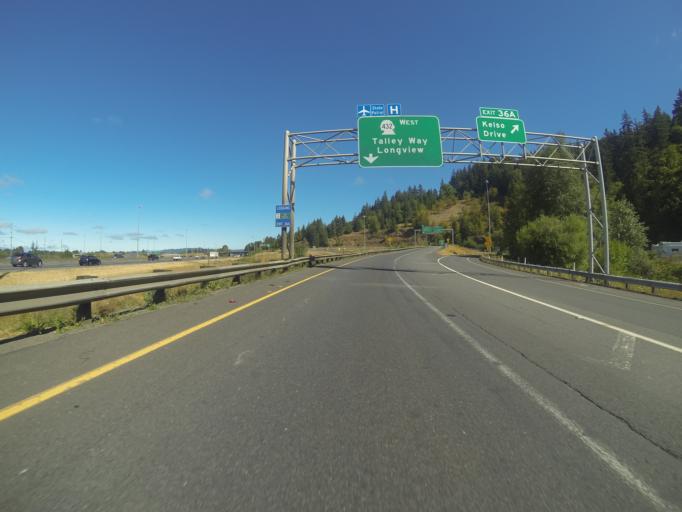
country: US
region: Washington
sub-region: Cowlitz County
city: Kelso
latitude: 46.1037
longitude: -122.8768
